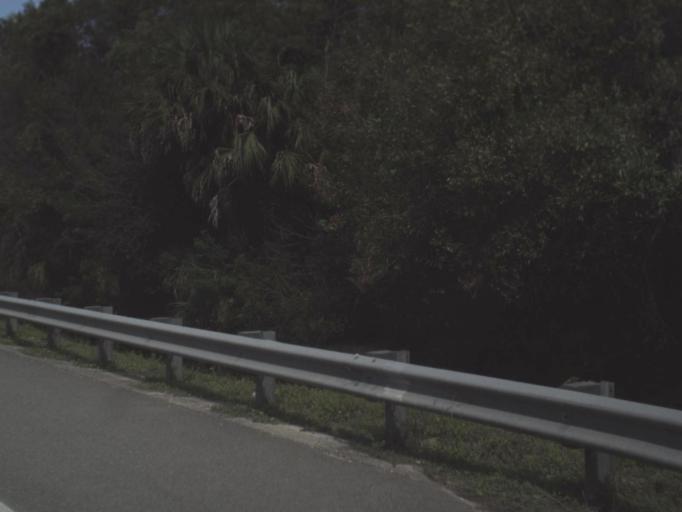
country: US
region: Florida
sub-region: Collier County
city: Lely Resort
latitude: 26.0489
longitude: -81.6764
